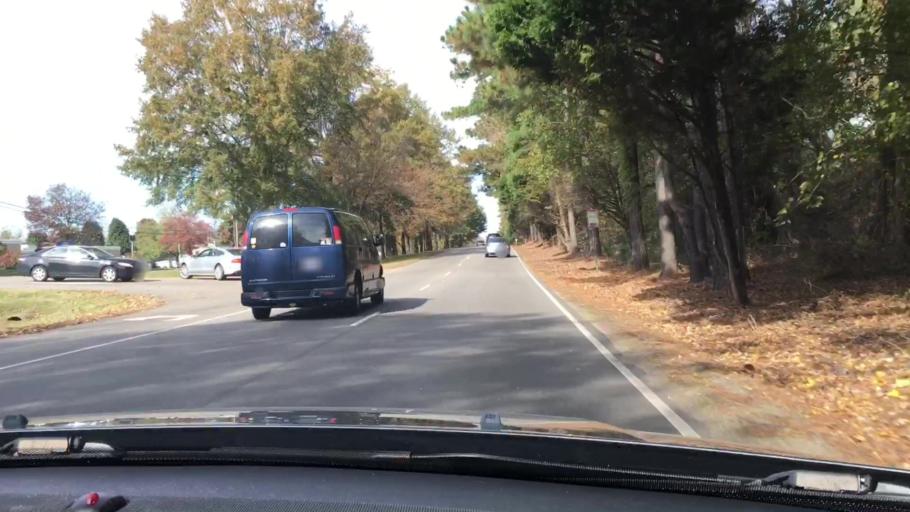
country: US
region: Virginia
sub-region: James City County
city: Williamsburg
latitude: 37.3052
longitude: -76.7287
